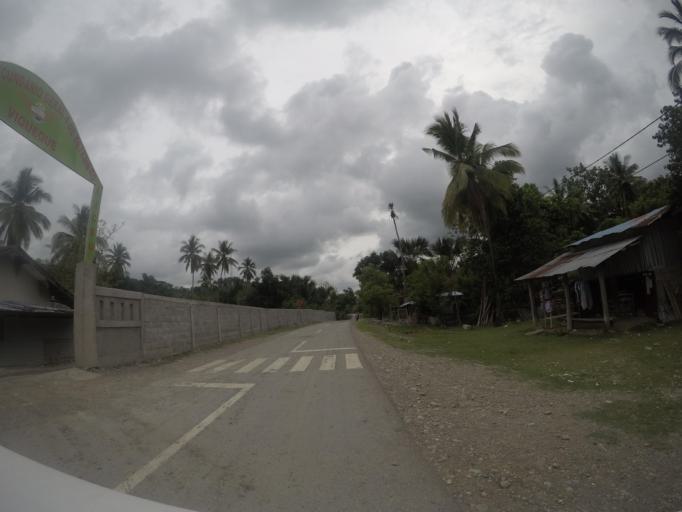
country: TL
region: Viqueque
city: Viqueque
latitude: -8.8575
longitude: 126.3680
